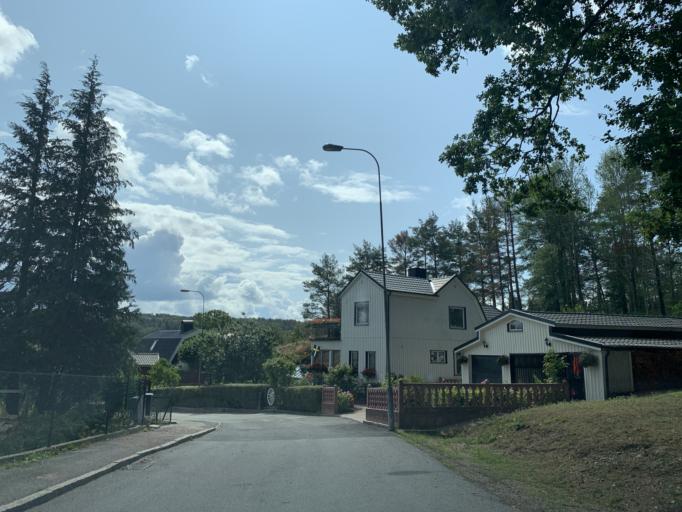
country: SE
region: Vaestra Goetaland
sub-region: Goteborg
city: Hammarkullen
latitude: 57.7733
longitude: 12.0325
